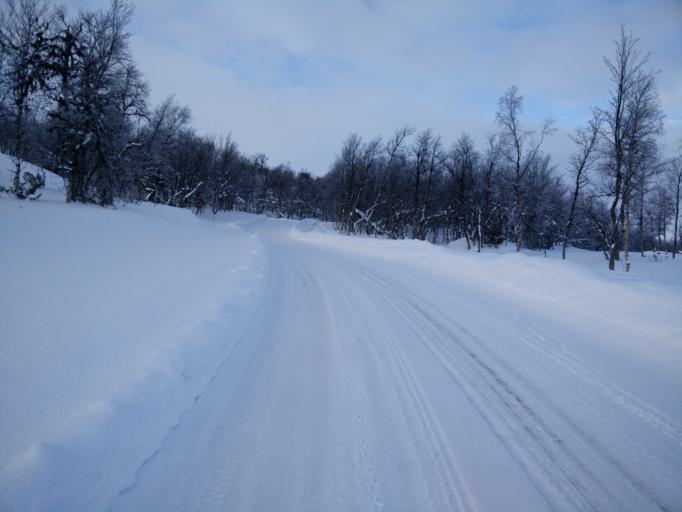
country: NO
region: Sor-Trondelag
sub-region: Tydal
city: Aas
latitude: 62.6515
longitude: 12.4002
